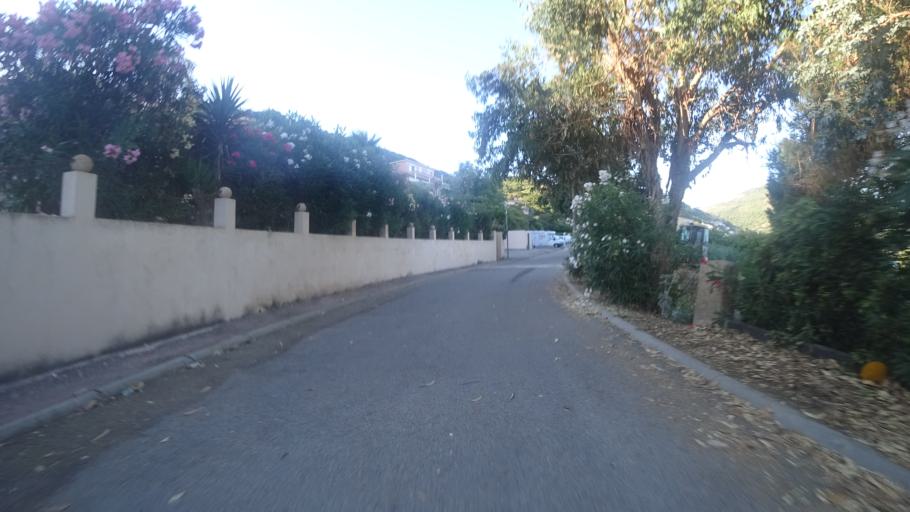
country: FR
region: Corsica
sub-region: Departement de la Corse-du-Sud
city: Alata
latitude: 41.9795
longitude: 8.6670
